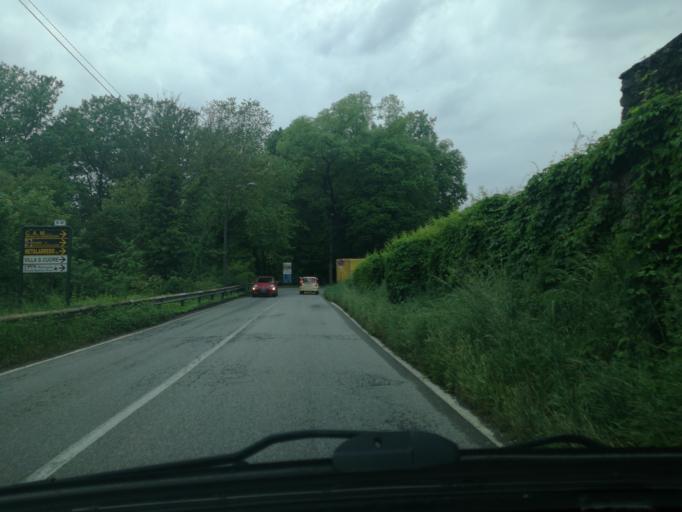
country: IT
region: Lombardy
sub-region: Provincia di Monza e Brianza
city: Canonica
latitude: 45.6483
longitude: 9.2826
